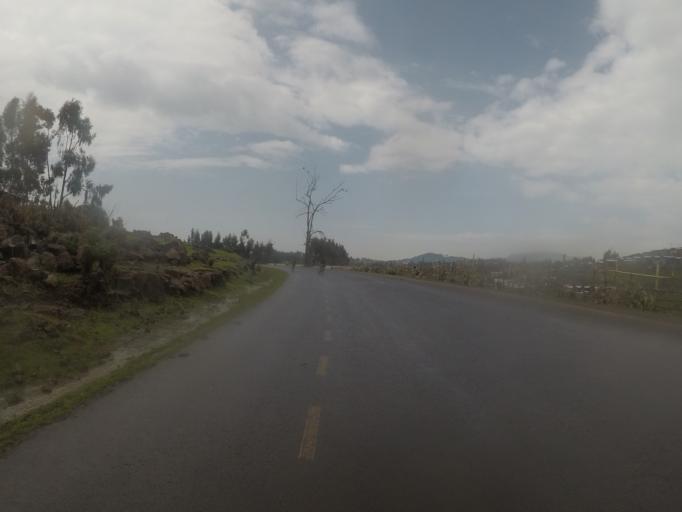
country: ET
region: Amhara
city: Debark'
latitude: 13.1387
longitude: 37.8944
